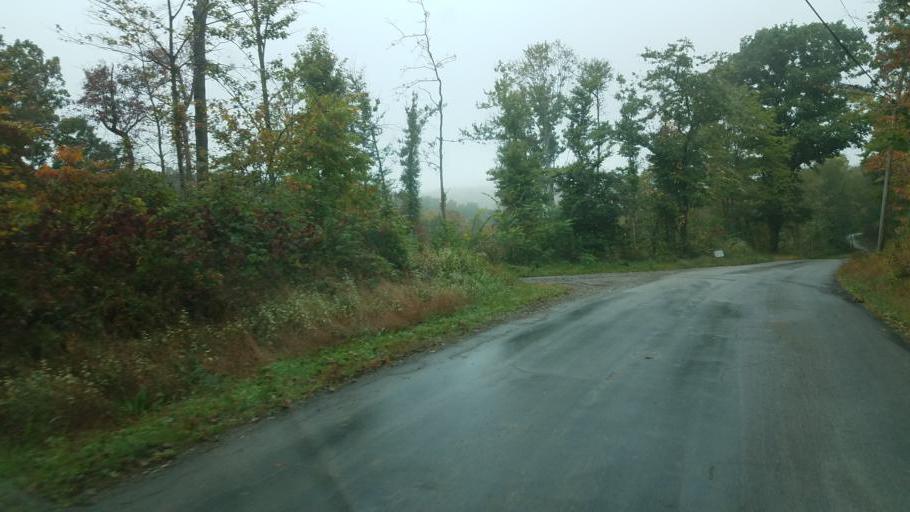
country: US
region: Ohio
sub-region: Harrison County
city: Cadiz
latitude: 40.3829
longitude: -81.0810
